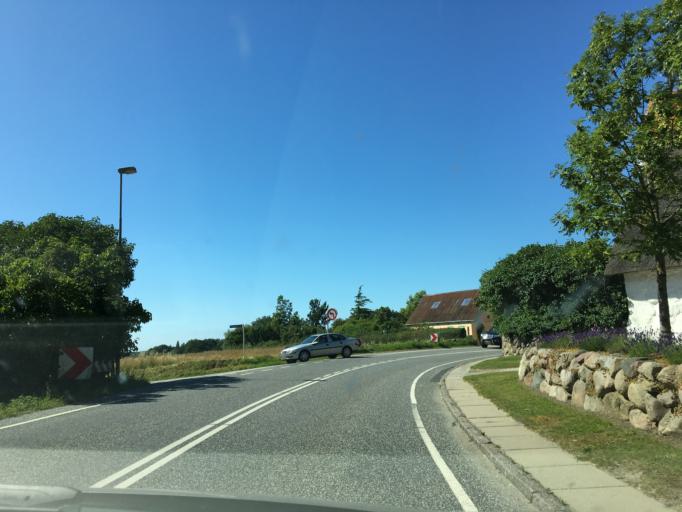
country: DK
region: South Denmark
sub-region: Langeland Kommune
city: Rudkobing
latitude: 54.8034
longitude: 10.7023
